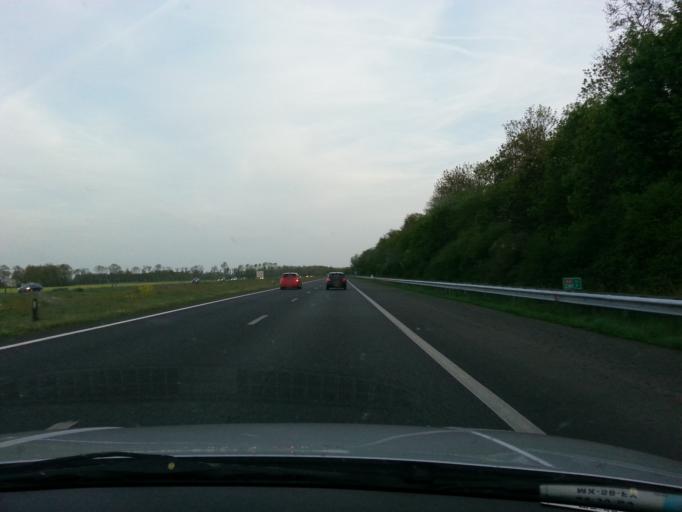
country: NL
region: Flevoland
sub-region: Gemeente Noordoostpolder
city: Emmeloord
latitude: 52.7556
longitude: 5.7664
